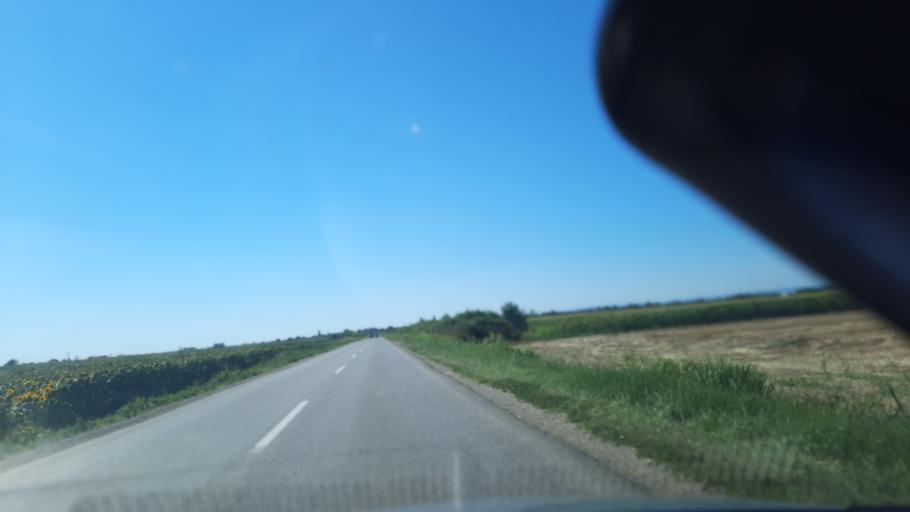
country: RS
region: Autonomna Pokrajina Vojvodina
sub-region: Sremski Okrug
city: Pecinci
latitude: 44.8906
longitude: 19.9845
